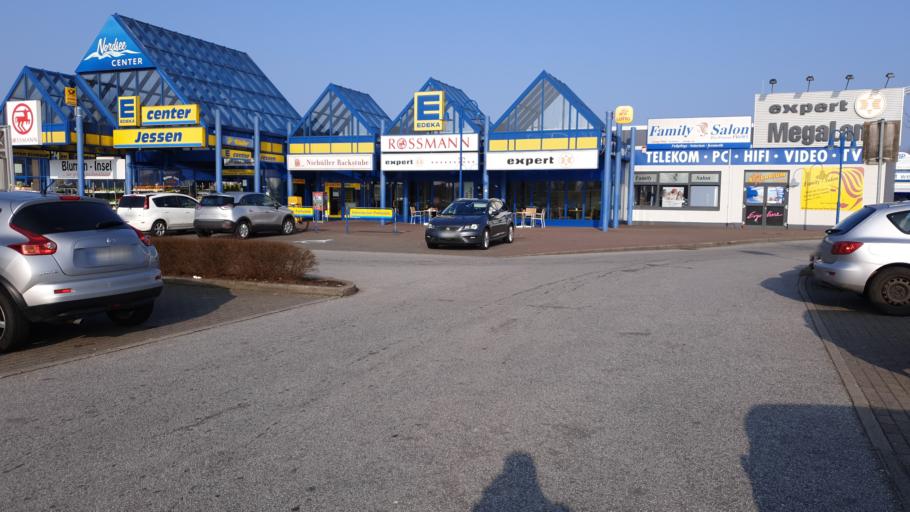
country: DE
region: Schleswig-Holstein
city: Husum
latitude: 54.4896
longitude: 9.0800
